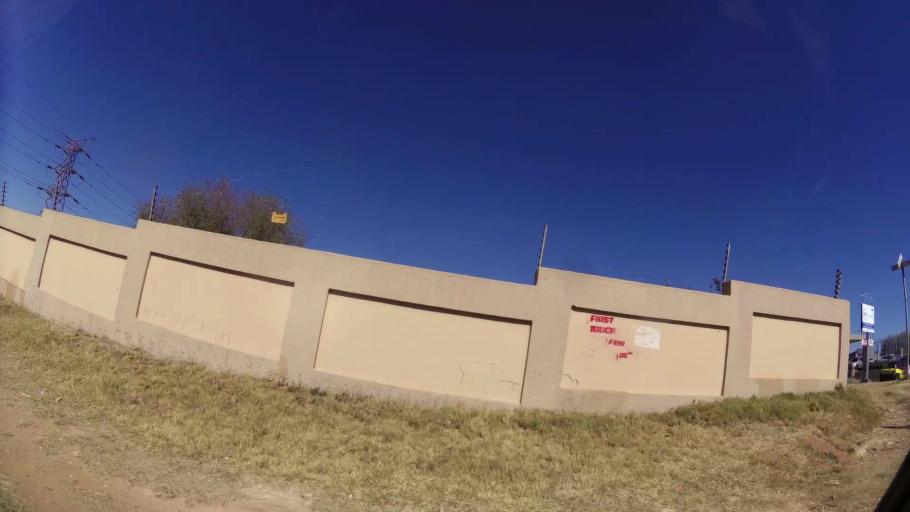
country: ZA
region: Gauteng
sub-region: City of Johannesburg Metropolitan Municipality
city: Johannesburg
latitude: -26.2696
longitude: 27.9889
